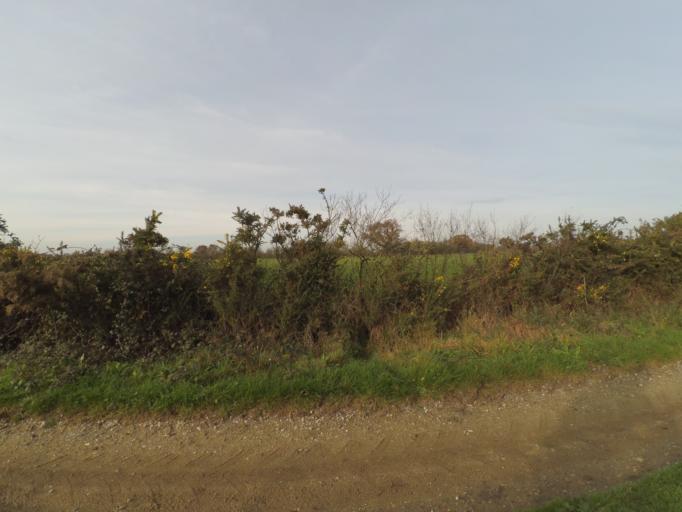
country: FR
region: Pays de la Loire
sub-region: Departement de la Loire-Atlantique
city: La Planche
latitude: 47.0051
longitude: -1.4021
